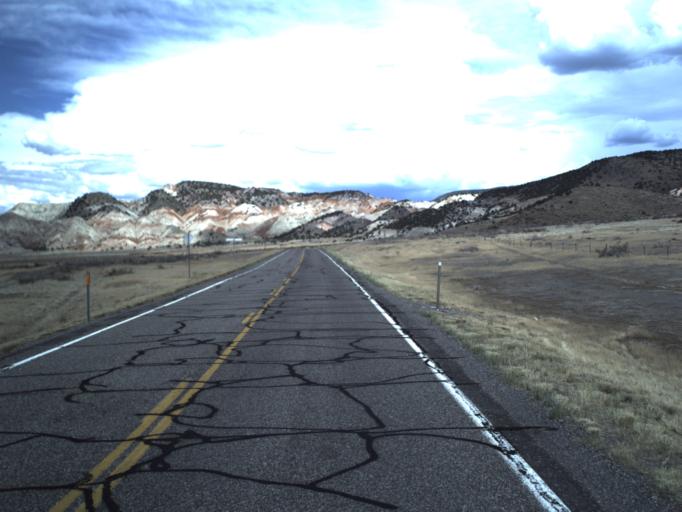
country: US
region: Utah
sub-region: Sevier County
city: Richfield
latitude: 38.7694
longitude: -111.9650
